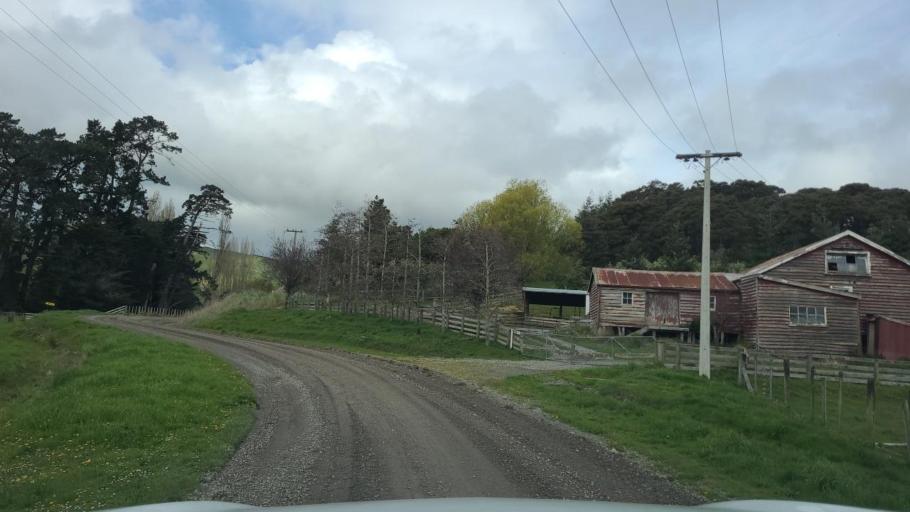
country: NZ
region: Wellington
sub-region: Masterton District
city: Masterton
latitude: -41.1561
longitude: 175.6086
